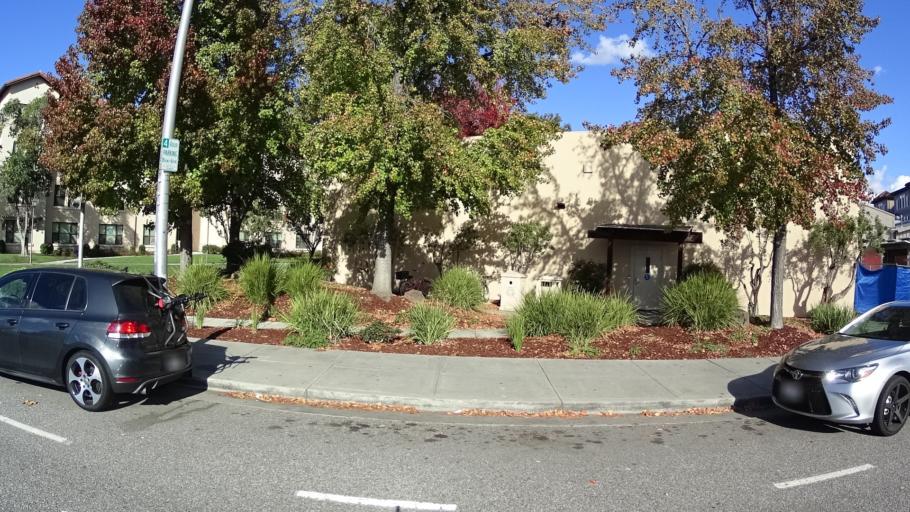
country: US
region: California
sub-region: Santa Clara County
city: Santa Clara
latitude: 37.3465
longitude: -121.9373
